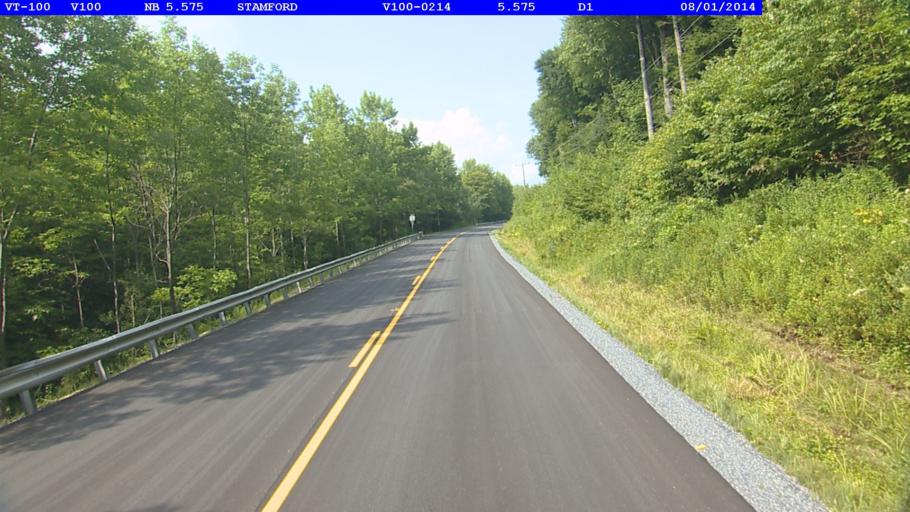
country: US
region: Massachusetts
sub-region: Berkshire County
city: North Adams
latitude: 42.8071
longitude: -73.0174
